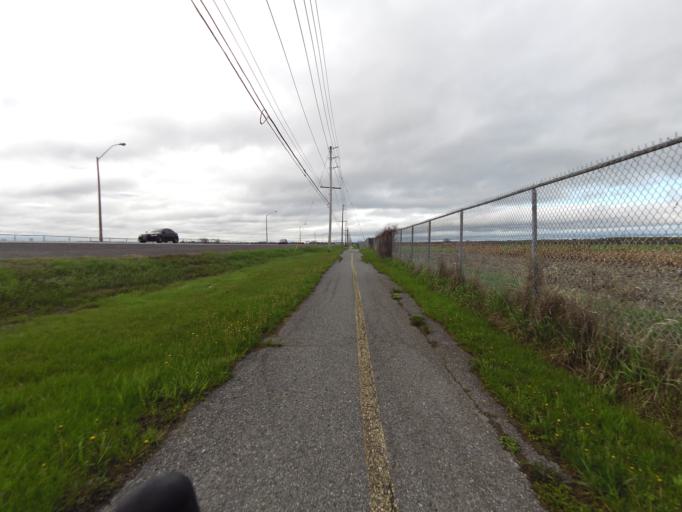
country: CA
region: Ontario
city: Bells Corners
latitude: 45.3127
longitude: -75.7716
